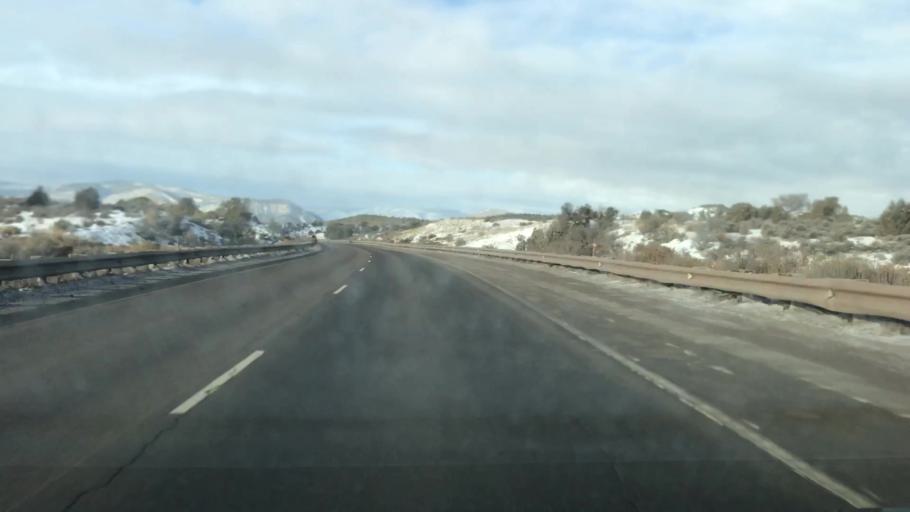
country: US
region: Colorado
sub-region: Eagle County
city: Eagle
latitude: 39.6542
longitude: -106.8667
